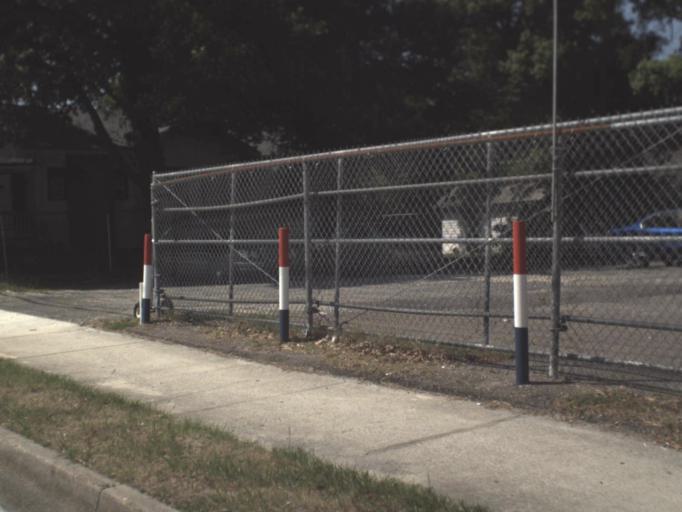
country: US
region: Florida
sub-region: Duval County
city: Jacksonville
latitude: 30.3775
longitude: -81.6684
